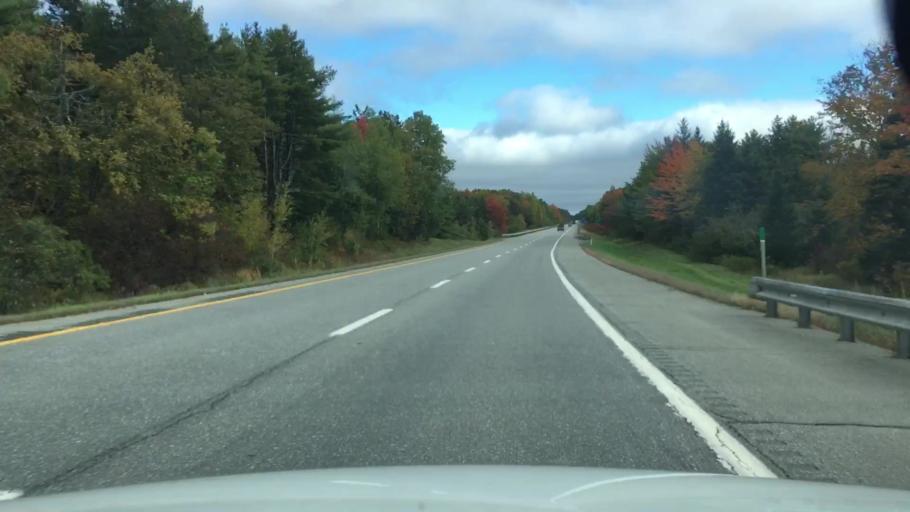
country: US
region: Maine
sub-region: Penobscot County
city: Carmel
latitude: 44.7696
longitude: -69.0007
